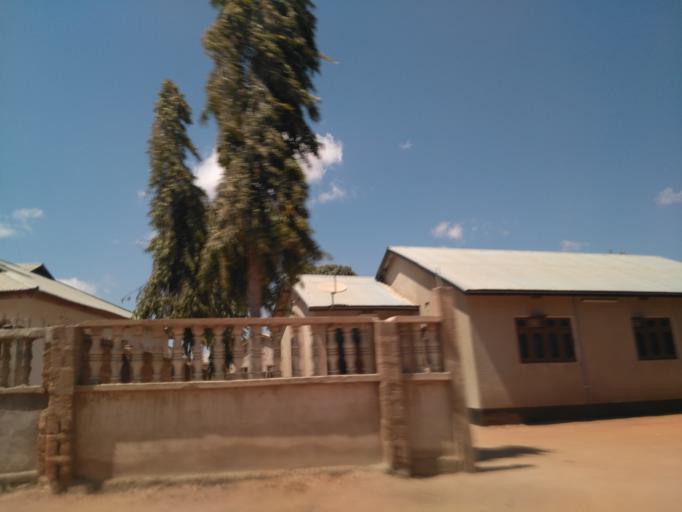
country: TZ
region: Dodoma
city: Kisasa
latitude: -6.1665
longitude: 35.7707
